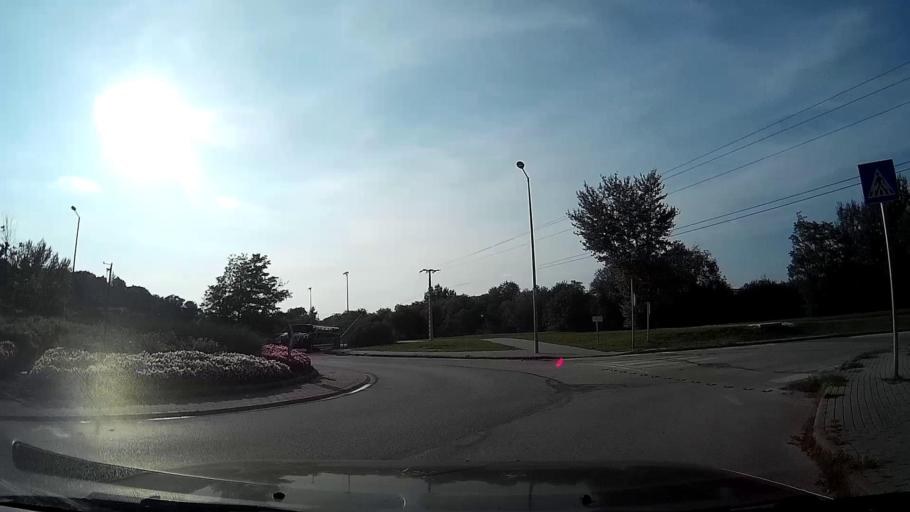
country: HU
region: Pest
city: Budaors
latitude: 47.4399
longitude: 18.9657
